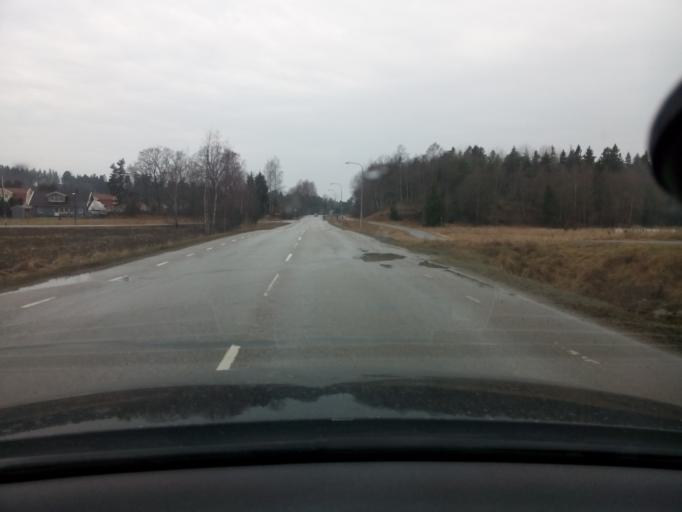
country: SE
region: Soedermanland
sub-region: Trosa Kommun
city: Trosa
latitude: 58.9018
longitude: 17.5680
